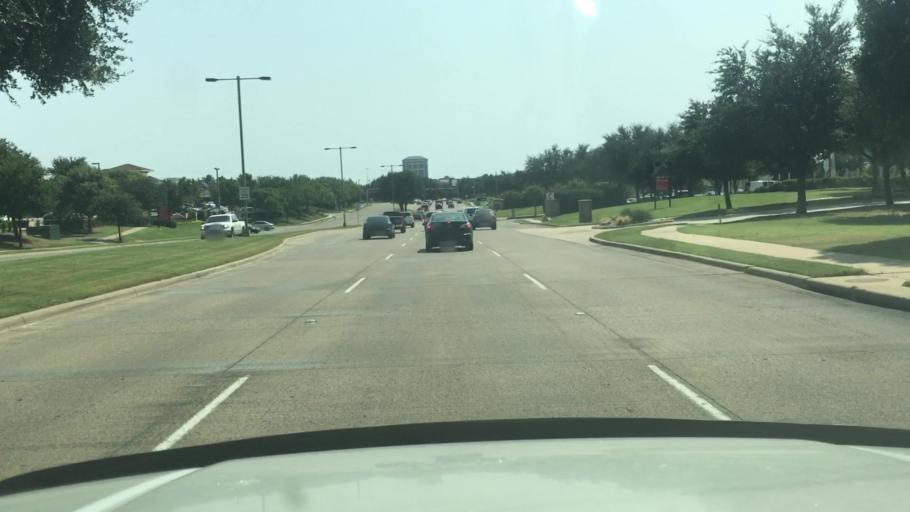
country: US
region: Texas
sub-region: Dallas County
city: Farmers Branch
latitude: 32.8991
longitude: -96.9589
